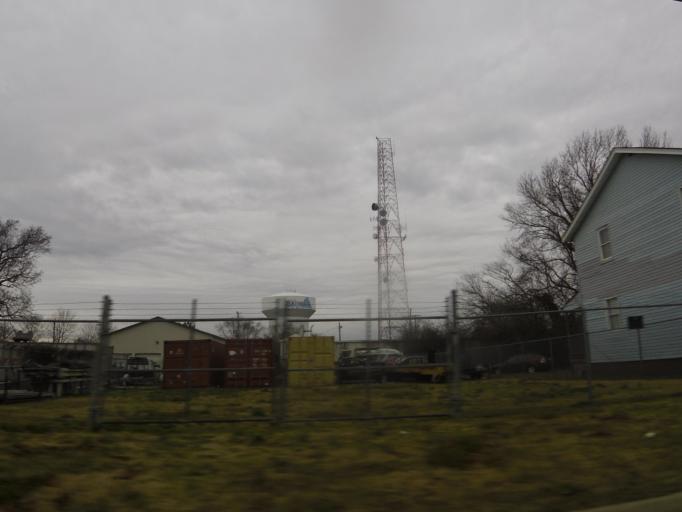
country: US
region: Virginia
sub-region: City of Portsmouth
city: Portsmouth
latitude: 36.8441
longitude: -76.3314
